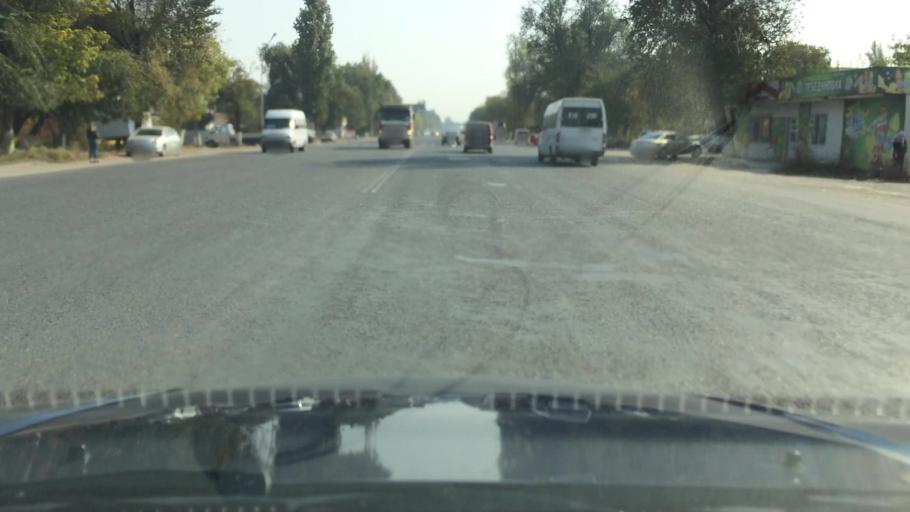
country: KG
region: Chuy
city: Lebedinovka
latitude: 42.8869
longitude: 74.6715
